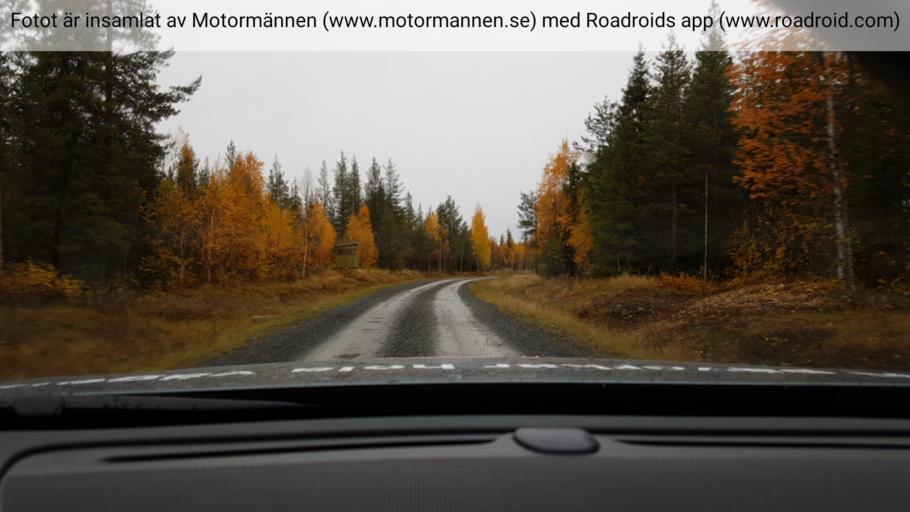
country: SE
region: Norrbotten
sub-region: Pajala Kommun
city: Pajala
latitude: 67.0093
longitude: 22.8527
